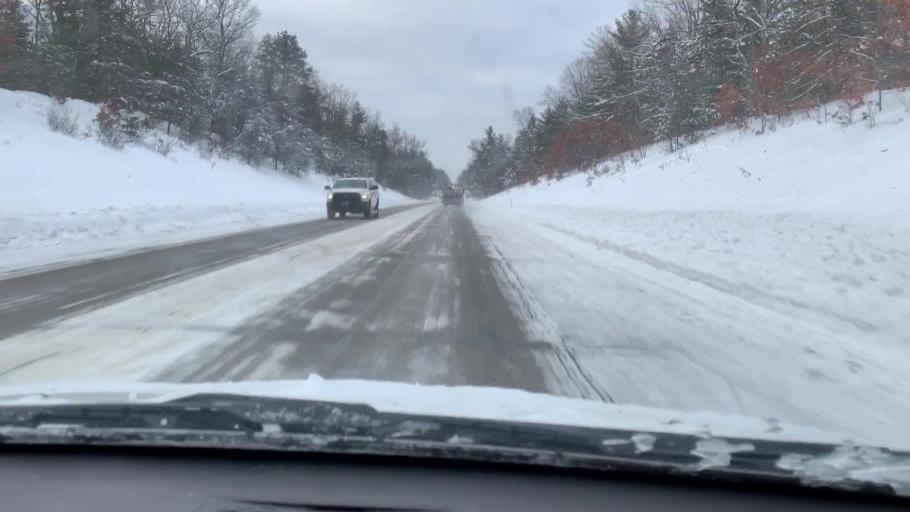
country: US
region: Michigan
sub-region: Wexford County
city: Manton
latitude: 44.5689
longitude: -85.3657
